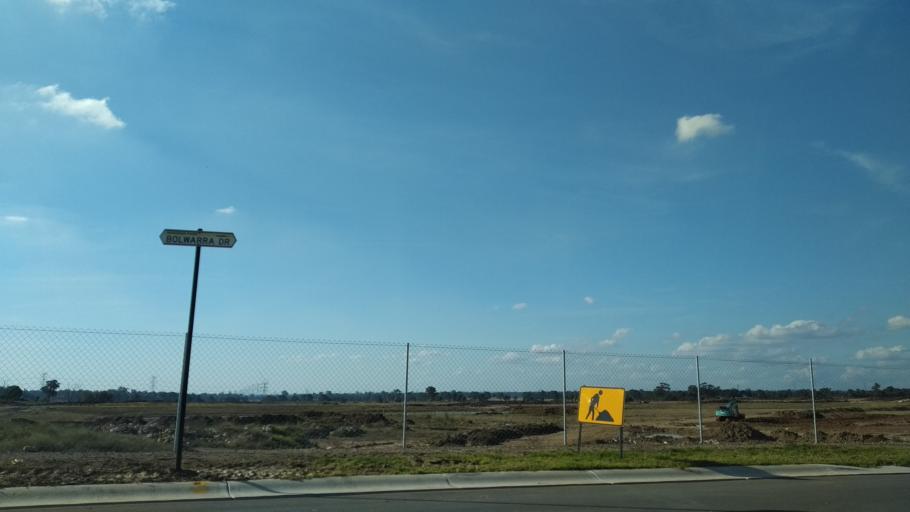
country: AU
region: New South Wales
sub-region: Blacktown
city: Blackett
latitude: -33.6901
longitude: 150.8098
